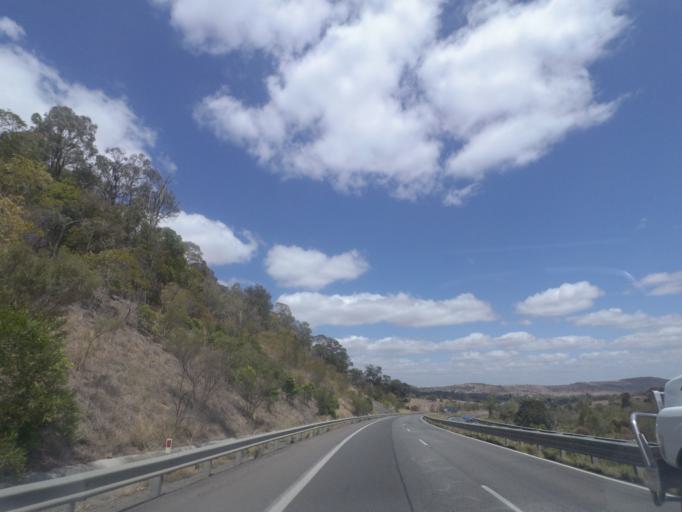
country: AU
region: Queensland
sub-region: Ipswich
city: Thagoona
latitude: -27.5645
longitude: 152.5575
